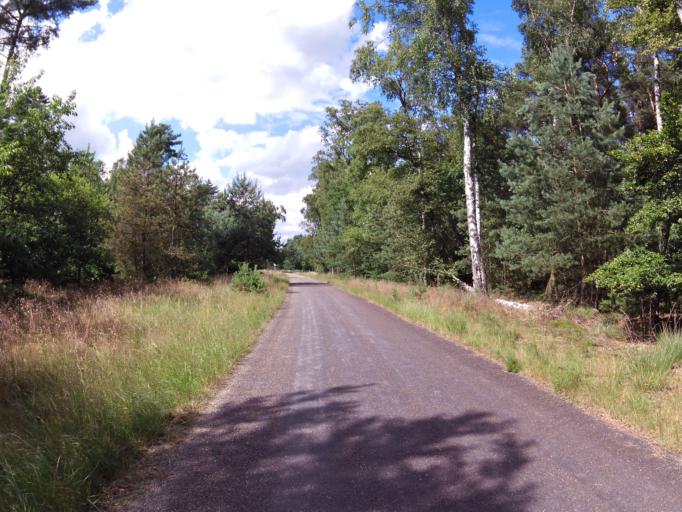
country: NL
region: North Brabant
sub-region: Gemeente Valkenswaard
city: Valkenswaard
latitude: 51.3159
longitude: 5.5112
